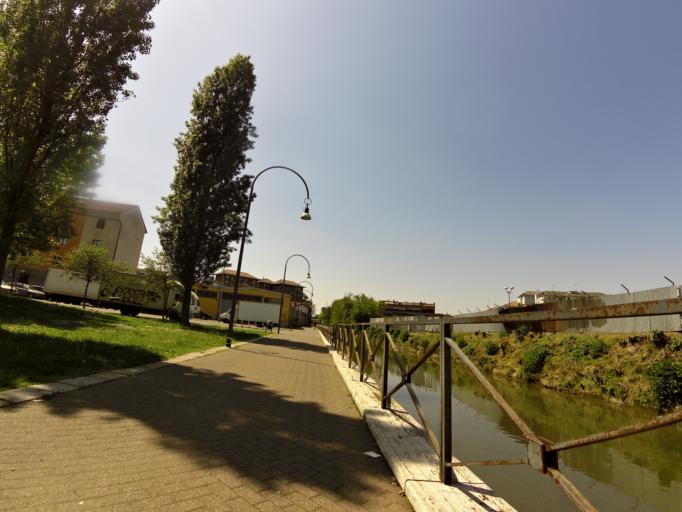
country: IT
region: Lombardy
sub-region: Citta metropolitana di Milano
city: Sesto San Giovanni
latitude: 45.5073
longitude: 9.2426
